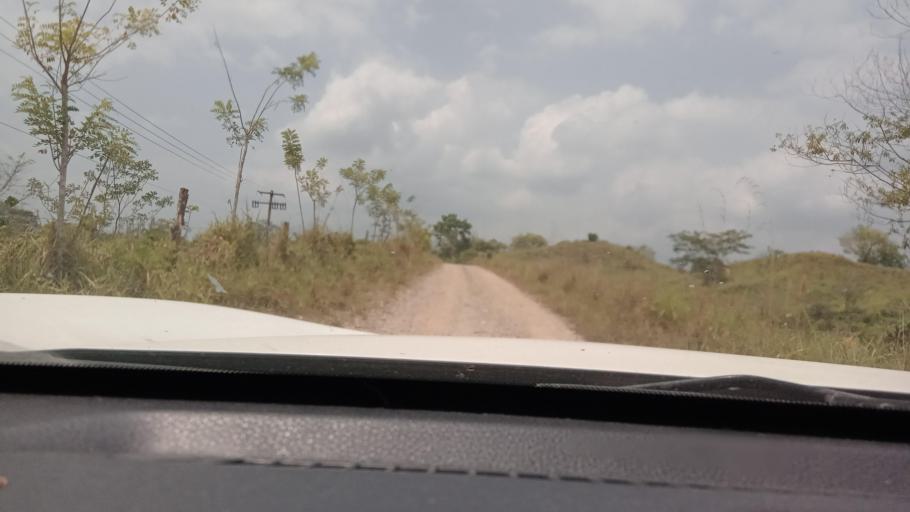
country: MX
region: Tabasco
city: Chontalpa
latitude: 17.5762
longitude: -93.7049
